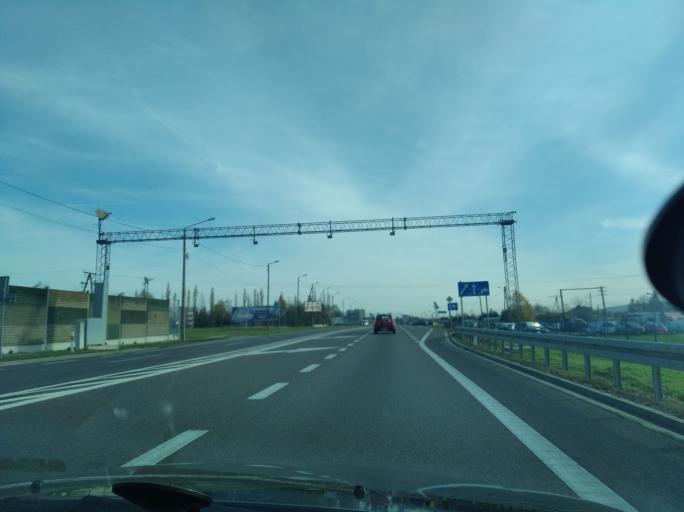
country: PL
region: Subcarpathian Voivodeship
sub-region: Powiat rzeszowski
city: Krasne
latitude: 50.0401
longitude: 22.0751
